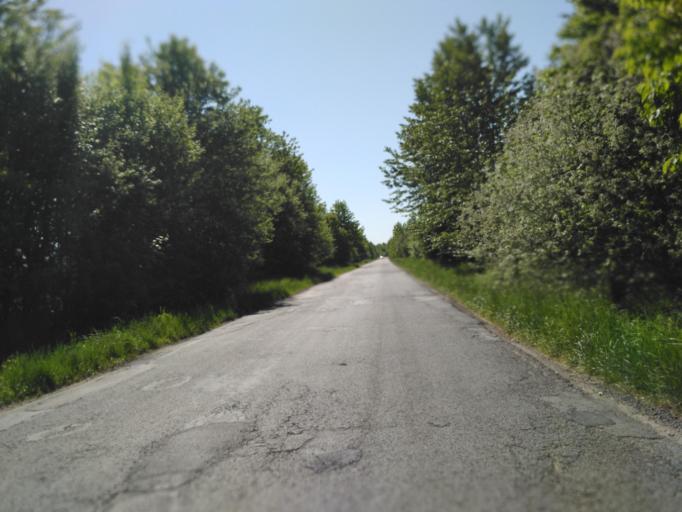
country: PL
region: Subcarpathian Voivodeship
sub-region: Krosno
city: Krosno
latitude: 49.6679
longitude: 21.7947
